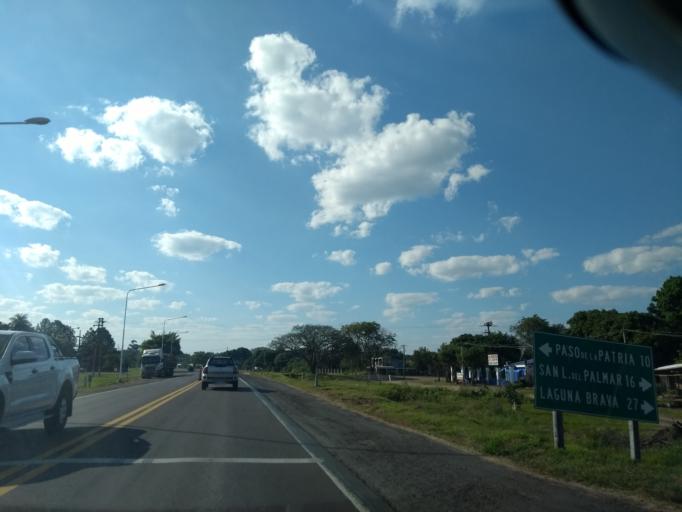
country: AR
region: Corrientes
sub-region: Departamento de San Cosme
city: San Cosme
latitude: -27.3906
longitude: -58.5547
